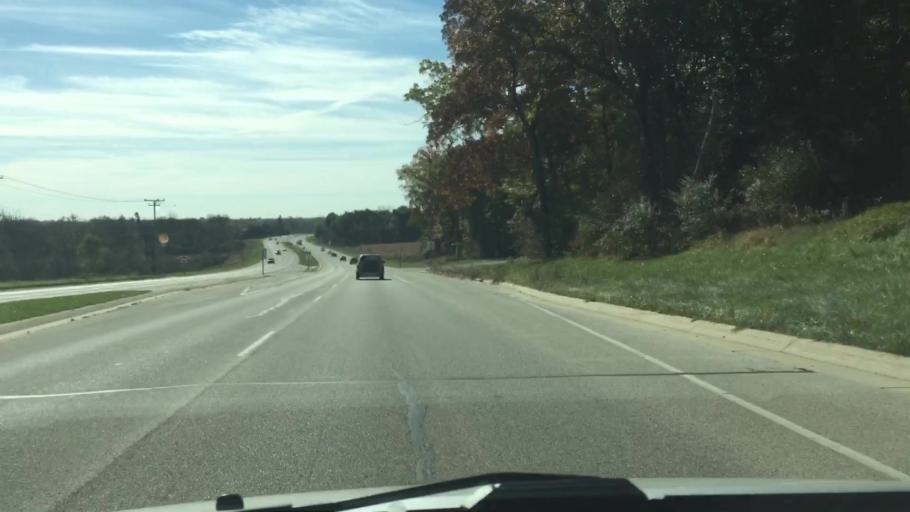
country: US
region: Wisconsin
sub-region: Waukesha County
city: Pewaukee
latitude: 43.1071
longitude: -88.2449
